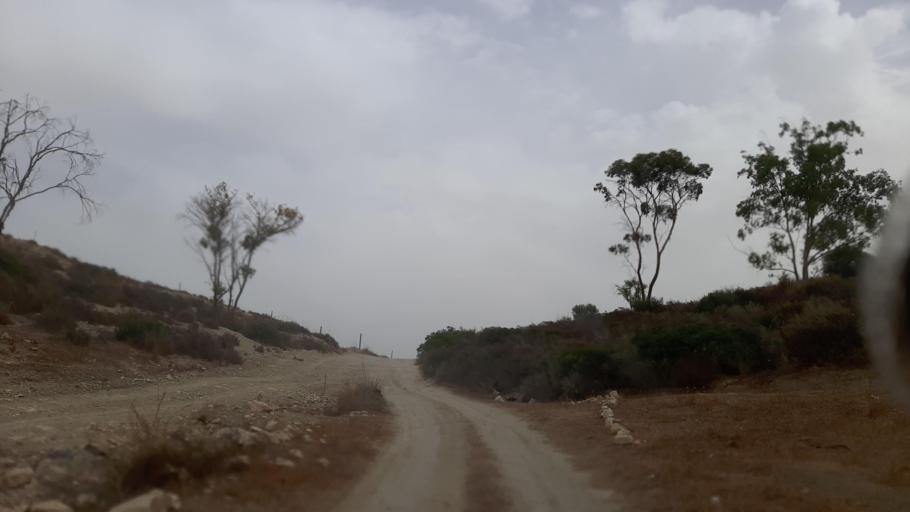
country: TN
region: Tunis
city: La Mohammedia
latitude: 36.5668
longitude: 10.1442
